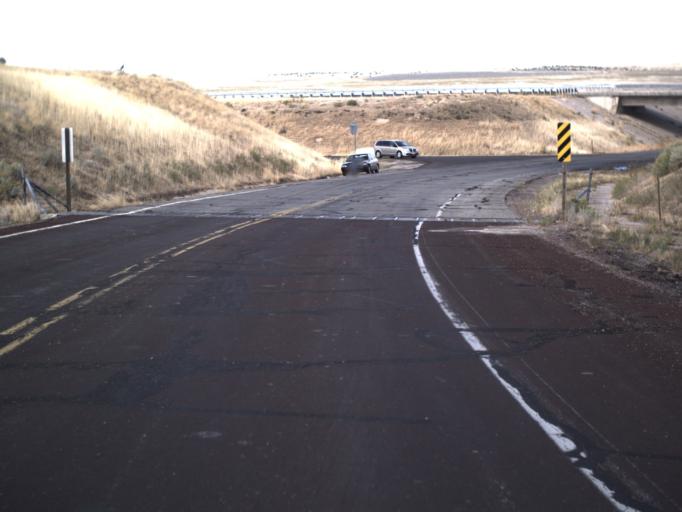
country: US
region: Utah
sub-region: Millard County
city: Fillmore
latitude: 38.7639
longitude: -112.5531
